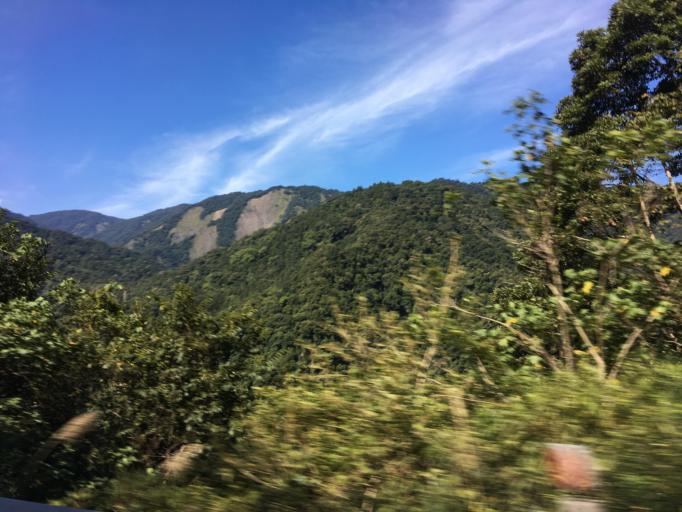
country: TW
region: Taiwan
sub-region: Yilan
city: Yilan
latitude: 24.5538
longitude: 121.5099
